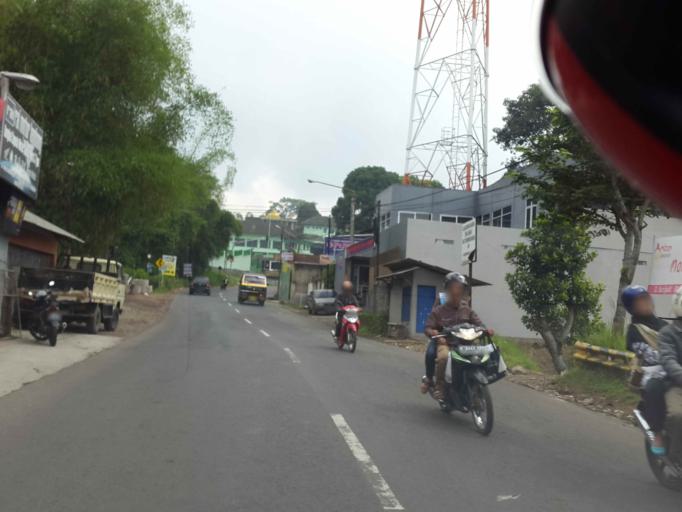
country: ID
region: West Java
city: Lembang
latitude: -6.8262
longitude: 107.6079
